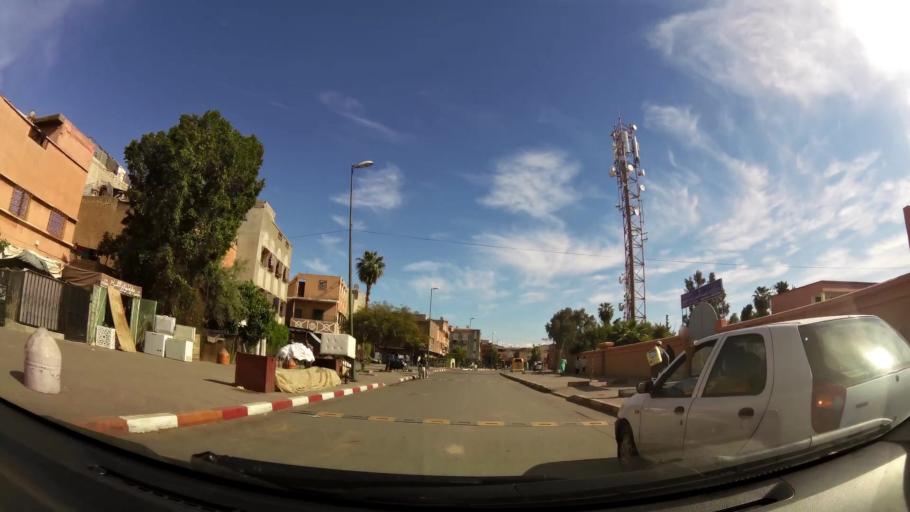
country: MA
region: Marrakech-Tensift-Al Haouz
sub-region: Marrakech
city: Marrakesh
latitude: 31.6089
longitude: -7.9613
